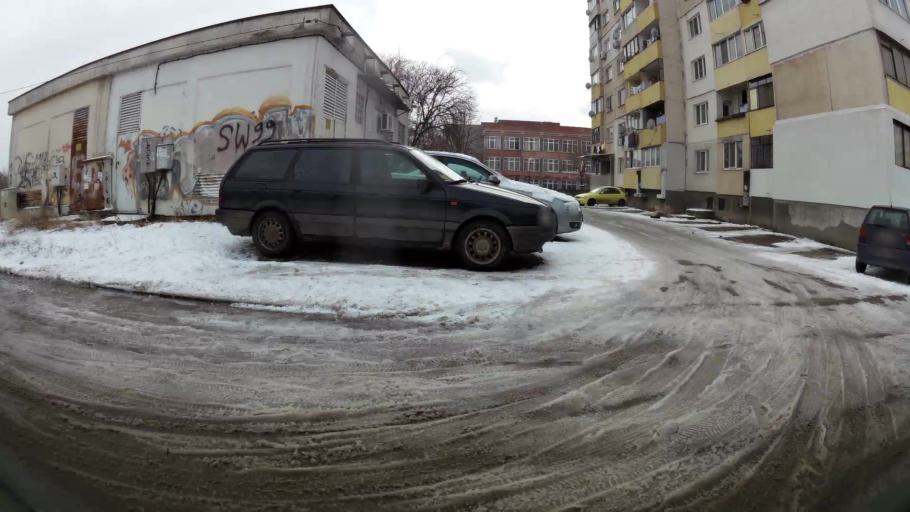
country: BG
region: Sofia-Capital
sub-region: Stolichna Obshtina
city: Sofia
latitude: 42.7148
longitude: 23.3780
